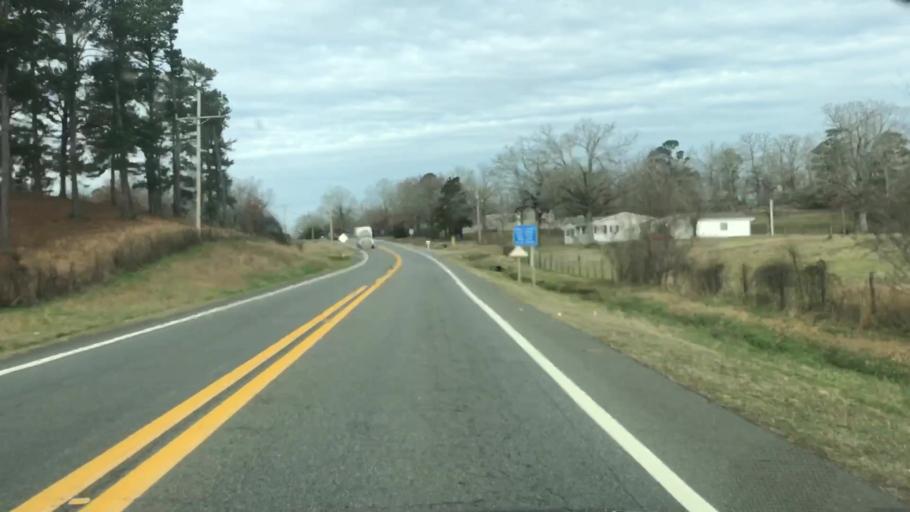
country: US
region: Arkansas
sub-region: Montgomery County
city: Mount Ida
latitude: 34.6231
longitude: -93.7258
